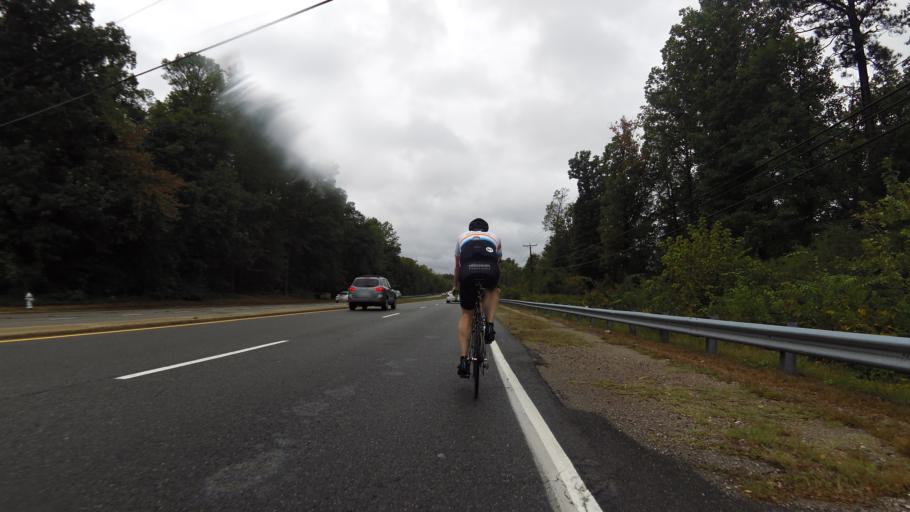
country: US
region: Virginia
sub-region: Henrico County
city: Short Pump
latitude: 37.5971
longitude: -77.6095
